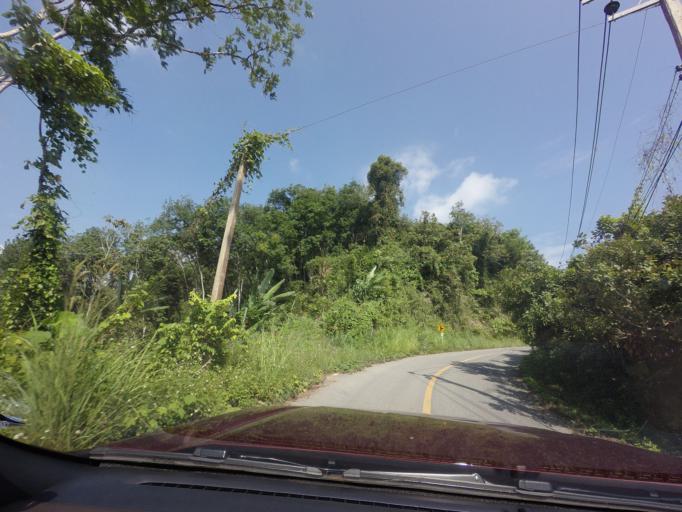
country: TH
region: Yala
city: Than To
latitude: 5.9946
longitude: 101.2111
